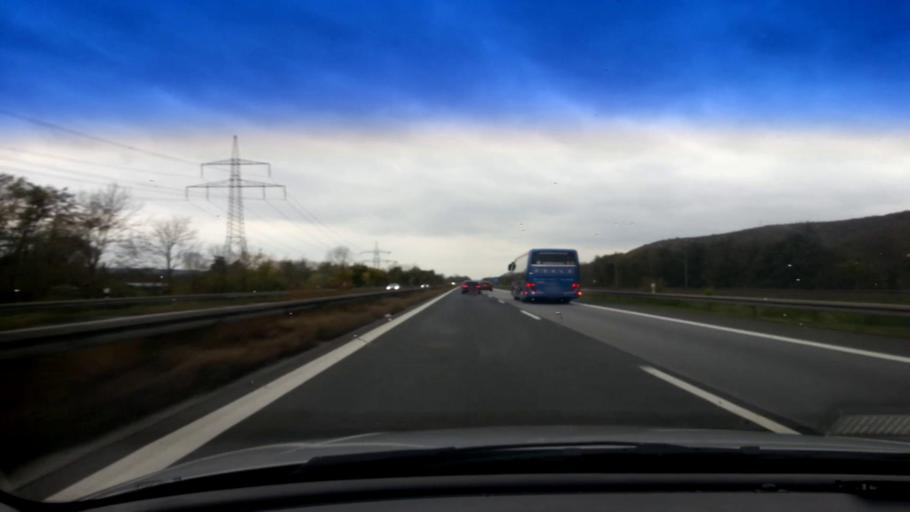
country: DE
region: Bavaria
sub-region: Regierungsbezirk Unterfranken
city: Stettfeld
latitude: 49.9731
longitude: 10.6990
